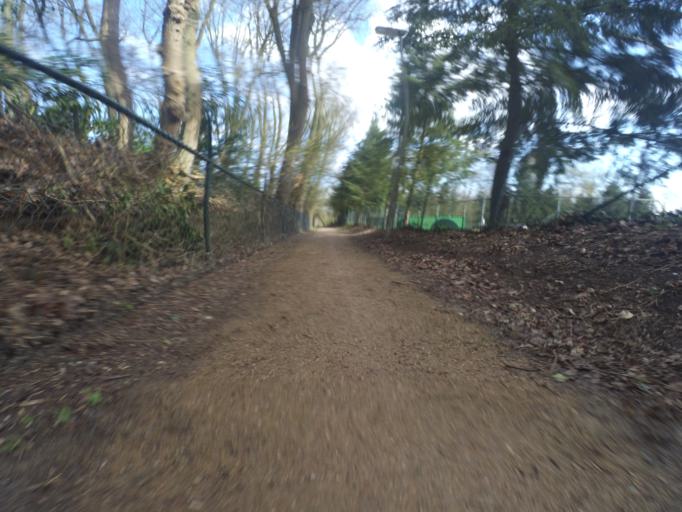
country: NL
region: Gelderland
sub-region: Gemeente Apeldoorn
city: Beekbergen
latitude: 52.1552
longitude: 5.9637
